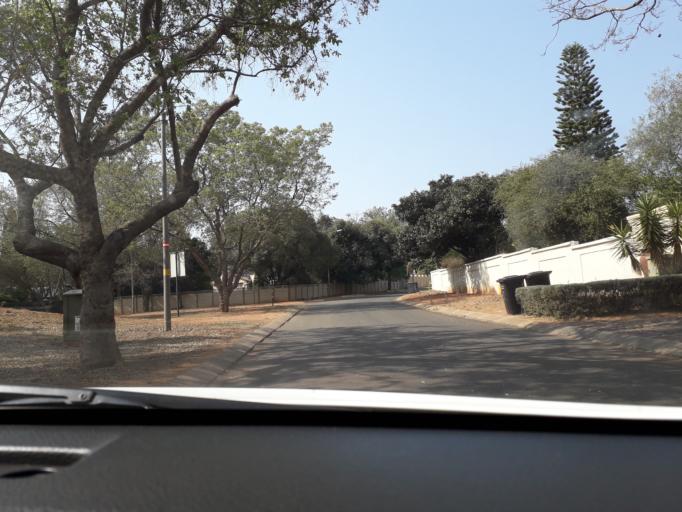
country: ZA
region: Gauteng
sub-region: City of Johannesburg Metropolitan Municipality
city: Modderfontein
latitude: -26.0760
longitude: 28.2391
